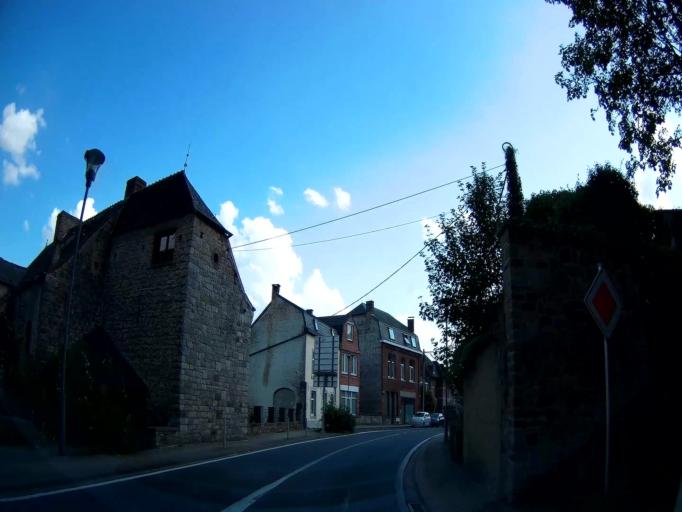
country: BE
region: Wallonia
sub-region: Province de Namur
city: Profondeville
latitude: 50.3482
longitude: 4.8519
